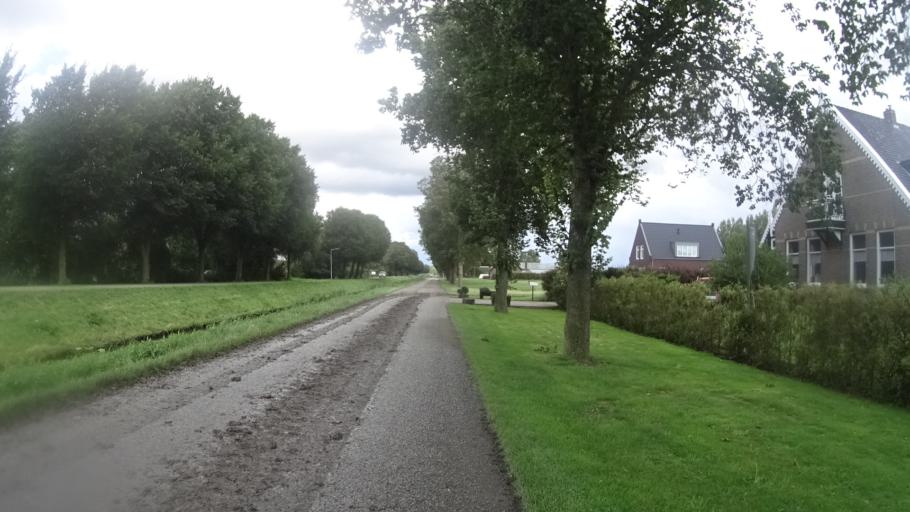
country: NL
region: North Holland
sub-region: Gemeente Schagen
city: Schagen
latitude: 52.8309
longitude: 4.8366
